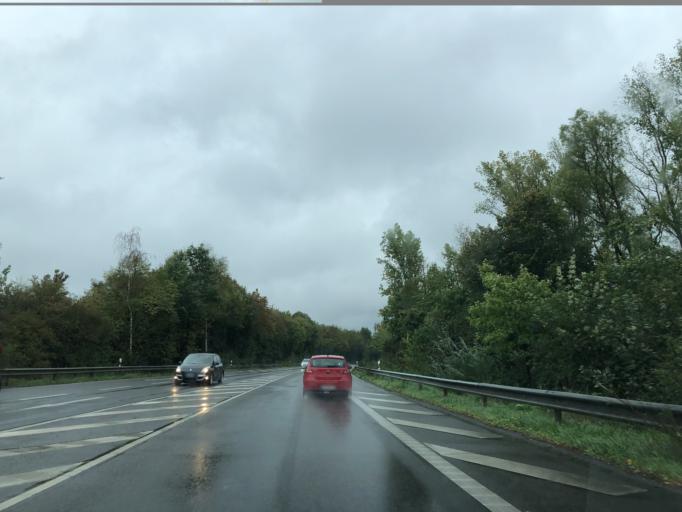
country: DE
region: North Rhine-Westphalia
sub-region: Regierungsbezirk Dusseldorf
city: Grevenbroich
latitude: 51.0588
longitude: 6.5618
